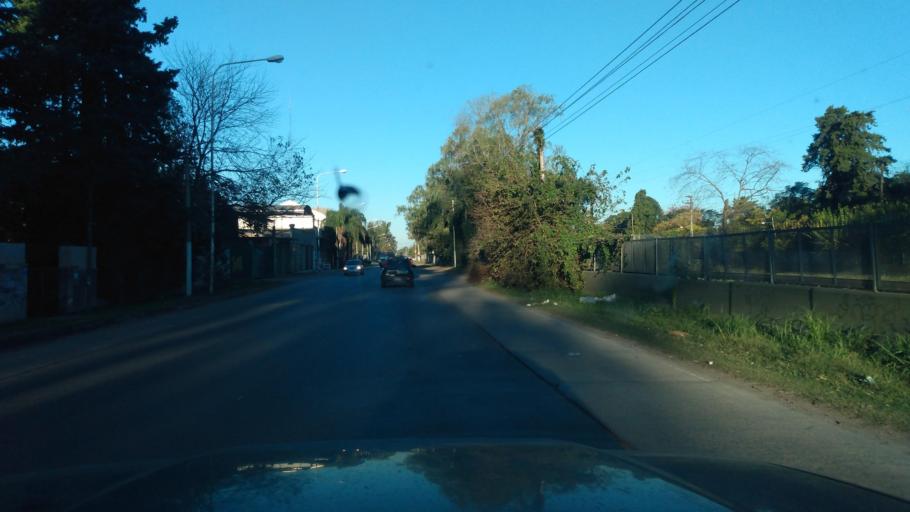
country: AR
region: Buenos Aires
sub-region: Partido de Merlo
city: Merlo
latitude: -34.6422
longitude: -58.8190
